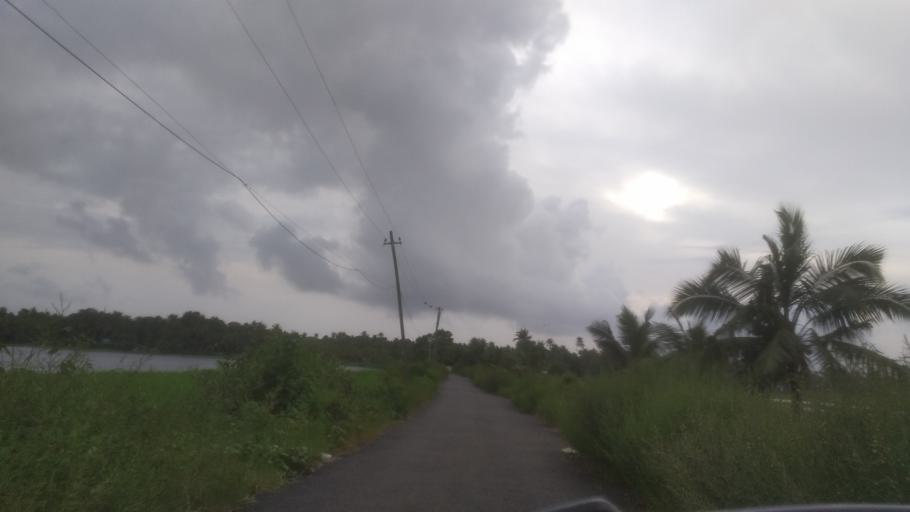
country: IN
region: Kerala
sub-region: Ernakulam
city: Elur
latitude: 10.0969
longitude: 76.2131
